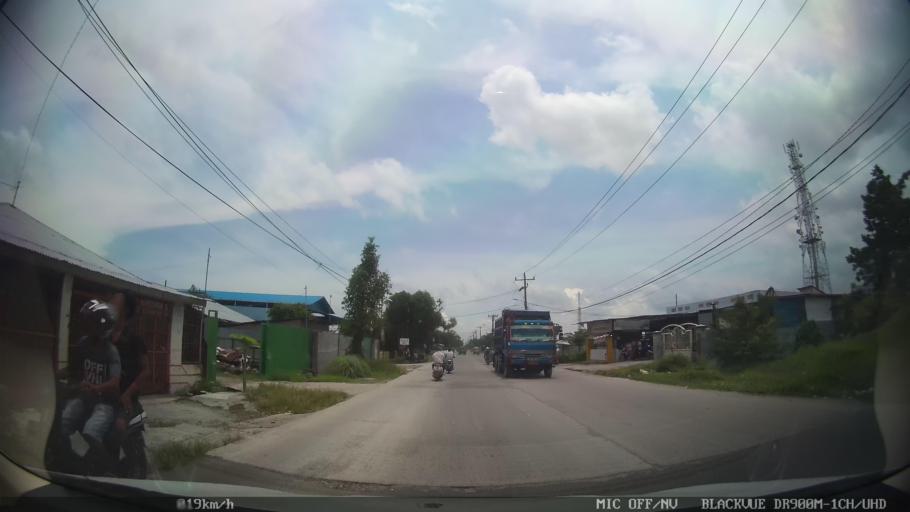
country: ID
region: North Sumatra
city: Labuhan Deli
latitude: 3.6908
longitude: 98.6828
